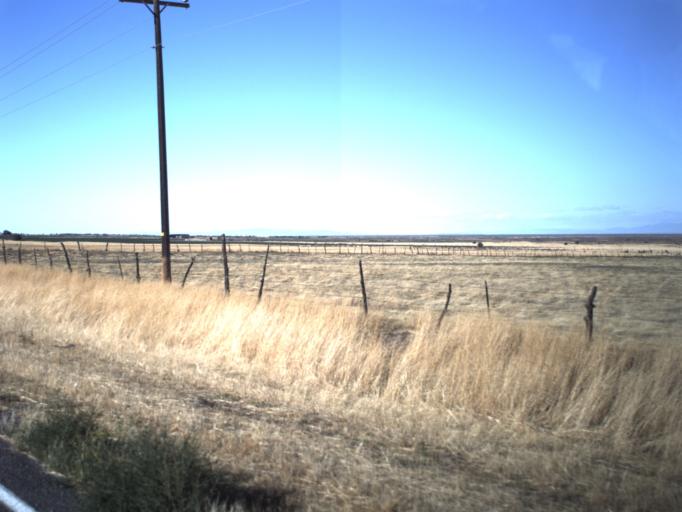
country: US
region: Utah
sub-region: Millard County
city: Delta
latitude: 39.4219
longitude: -112.3278
